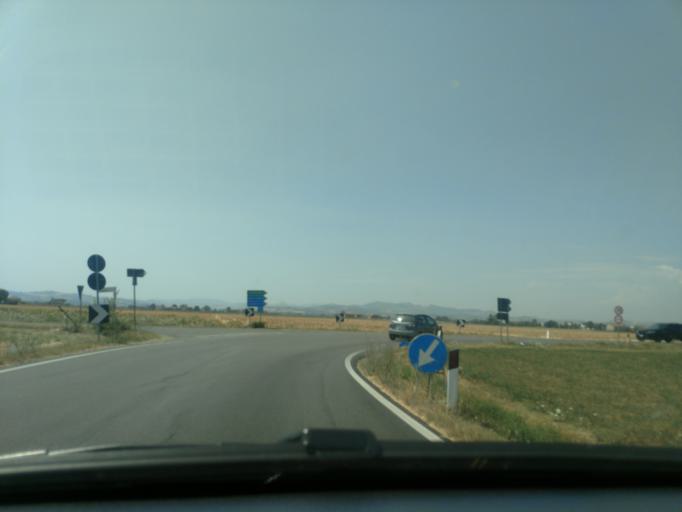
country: IT
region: Emilia-Romagna
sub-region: Provincia di Bologna
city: Medicina-Buda
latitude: 44.4373
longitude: 11.6286
